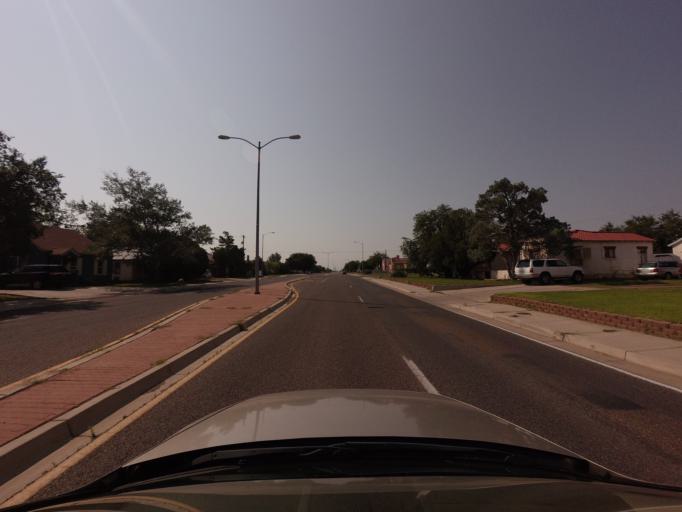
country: US
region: New Mexico
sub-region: Quay County
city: Tucumcari
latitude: 35.1684
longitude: -103.7250
